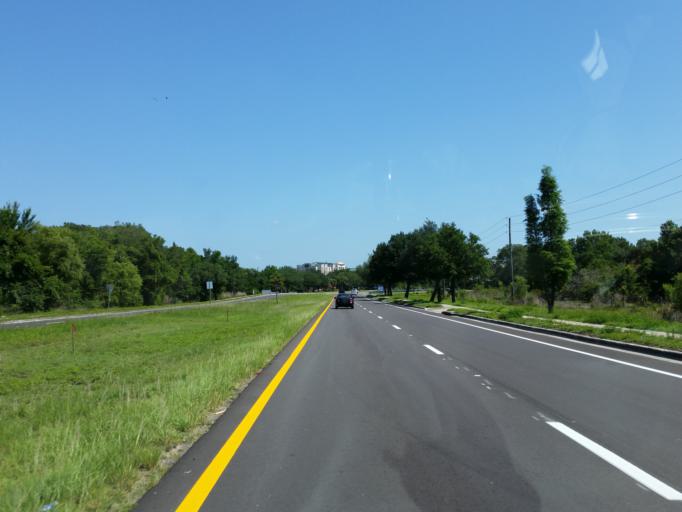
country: US
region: Florida
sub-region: Hillsborough County
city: Palm River-Clair Mel
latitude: 27.9351
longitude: -82.3380
